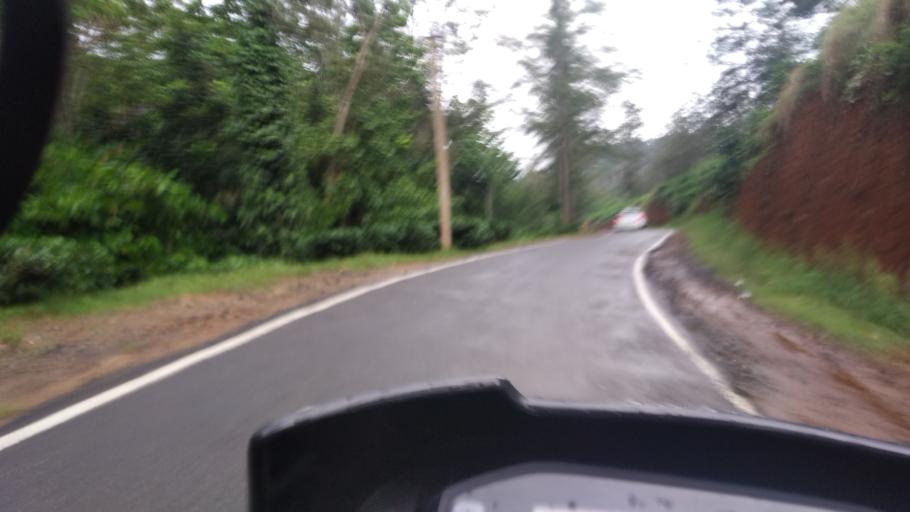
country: IN
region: Tamil Nadu
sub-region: Theni
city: Gudalur
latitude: 9.5686
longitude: 77.0796
